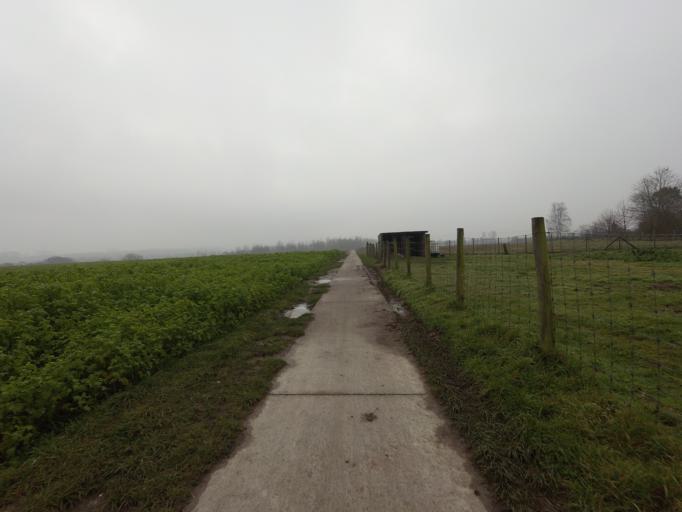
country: BE
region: Flanders
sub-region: Provincie Oost-Vlaanderen
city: Ninove
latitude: 50.8328
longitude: 4.0010
